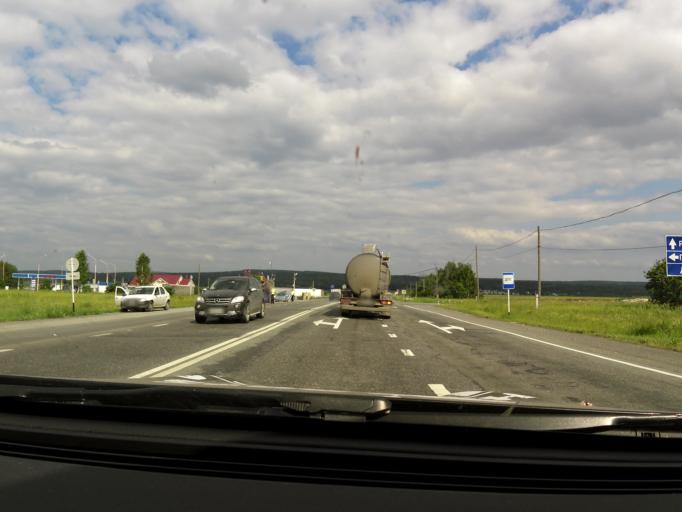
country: RU
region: Sverdlovsk
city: Druzhinino
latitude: 56.8109
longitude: 59.5249
